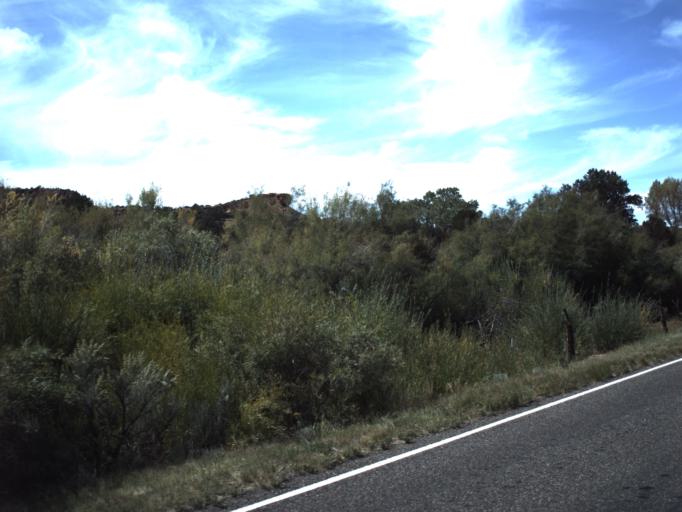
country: US
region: Utah
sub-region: Wayne County
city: Loa
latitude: 38.2800
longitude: -111.3883
